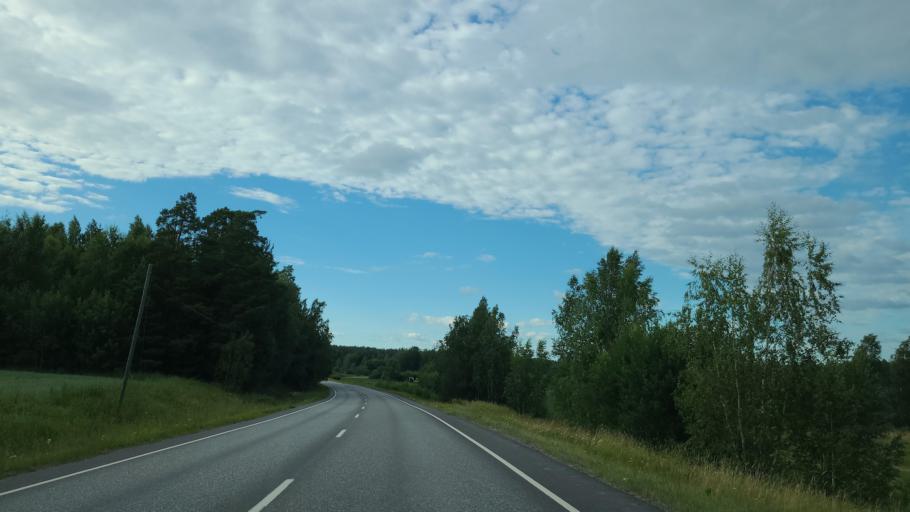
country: FI
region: Varsinais-Suomi
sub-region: Turku
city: Merimasku
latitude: 60.4255
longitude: 21.8973
